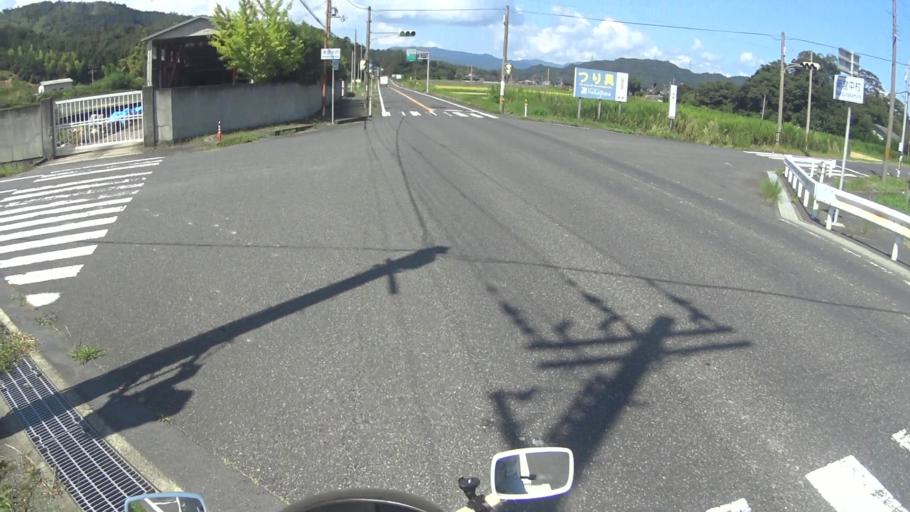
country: JP
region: Kyoto
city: Miyazu
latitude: 35.5358
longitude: 135.2400
